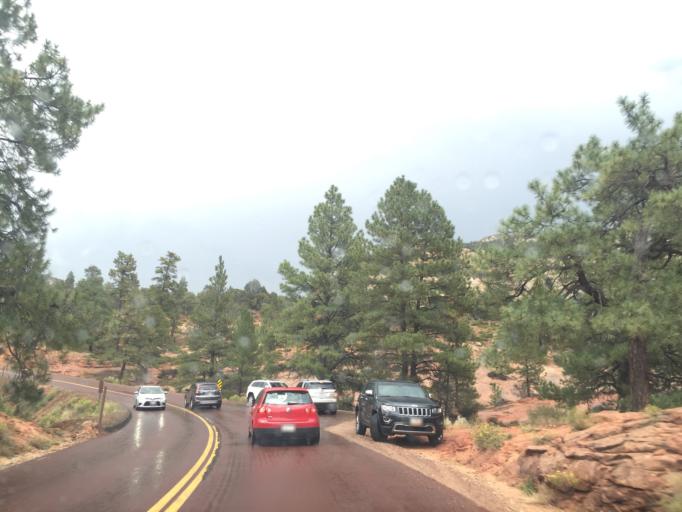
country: US
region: Utah
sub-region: Washington County
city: Hildale
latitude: 37.2275
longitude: -112.8798
